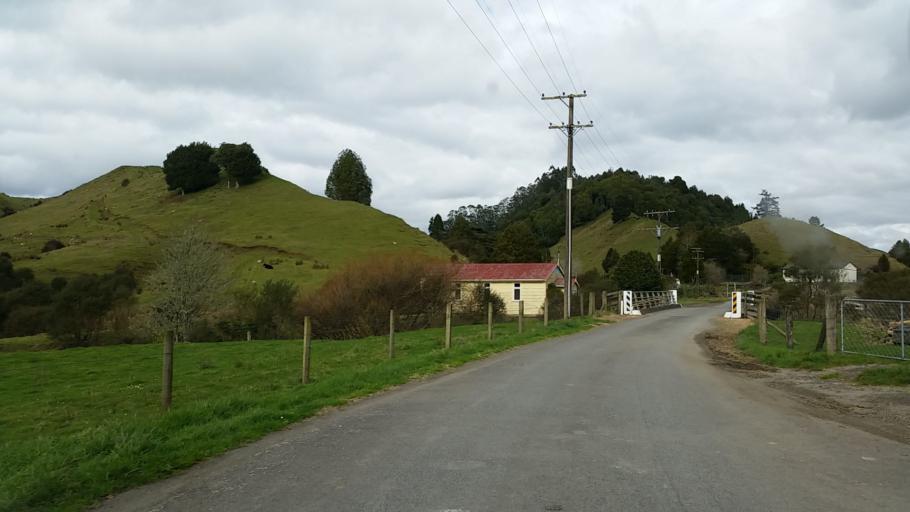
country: NZ
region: Taranaki
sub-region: New Plymouth District
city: Waitara
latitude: -39.1586
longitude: 174.5626
